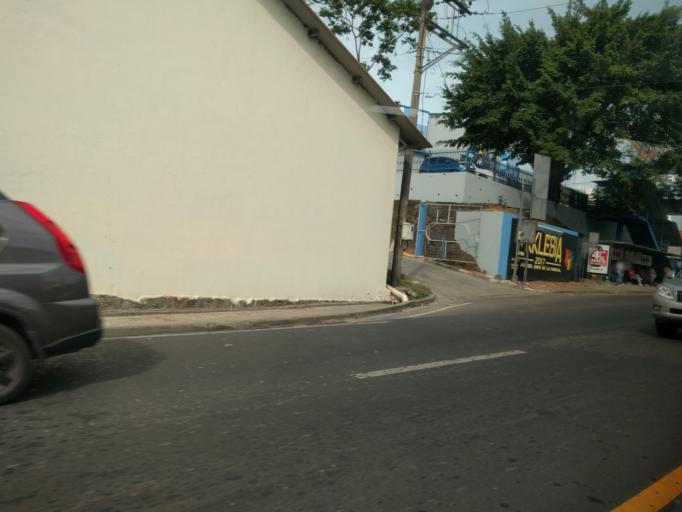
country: PA
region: Panama
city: Panama
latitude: 8.9775
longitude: -79.5352
